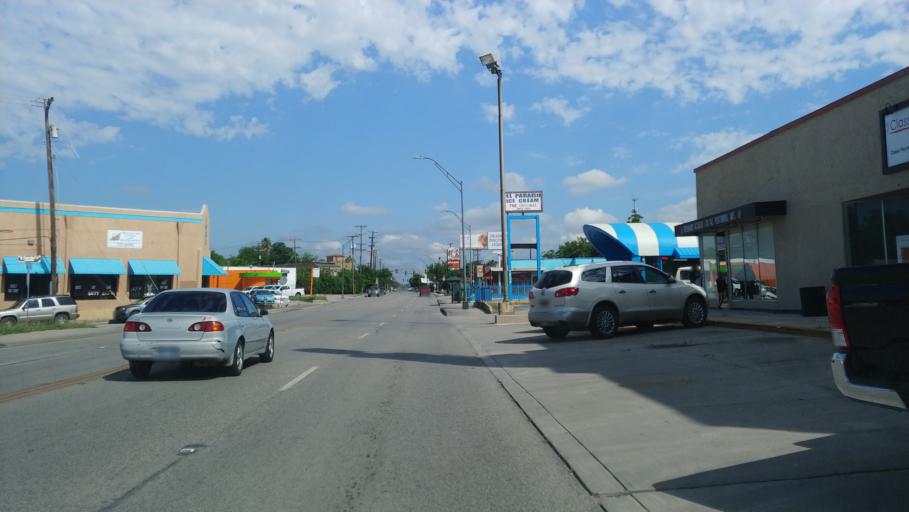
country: US
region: Texas
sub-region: Bexar County
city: Balcones Heights
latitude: 29.4632
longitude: -98.5246
